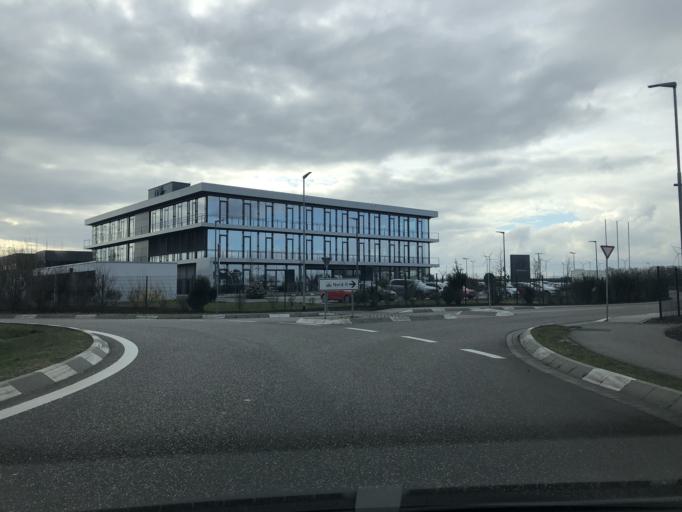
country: DE
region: Rheinland-Pfalz
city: Rulzheim
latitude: 49.1662
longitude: 8.2977
